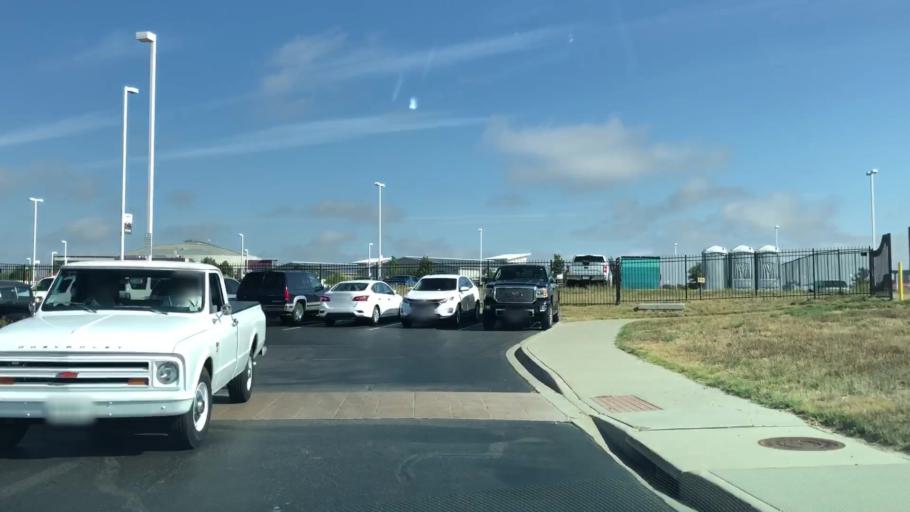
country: US
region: Colorado
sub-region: Weld County
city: Windsor
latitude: 40.4406
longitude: -104.9884
